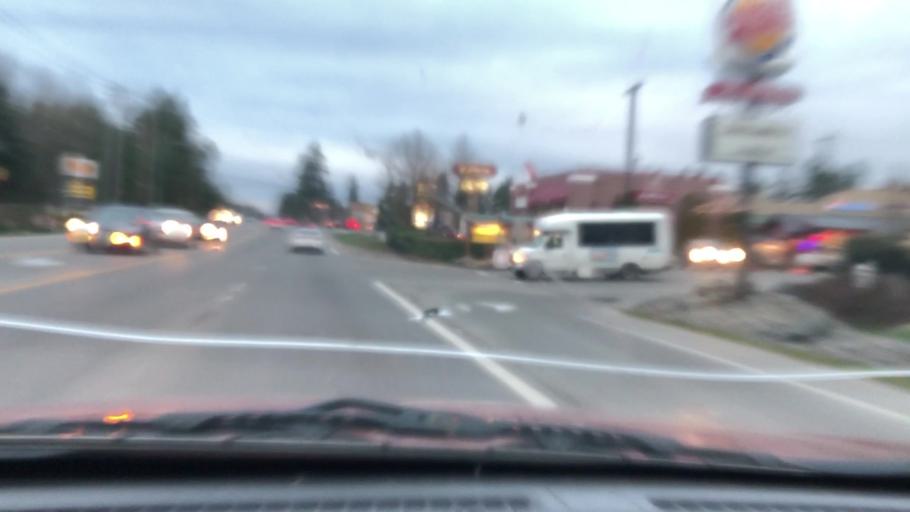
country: US
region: Washington
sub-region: Pierce County
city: Elk Plain
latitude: 47.0548
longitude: -122.3994
